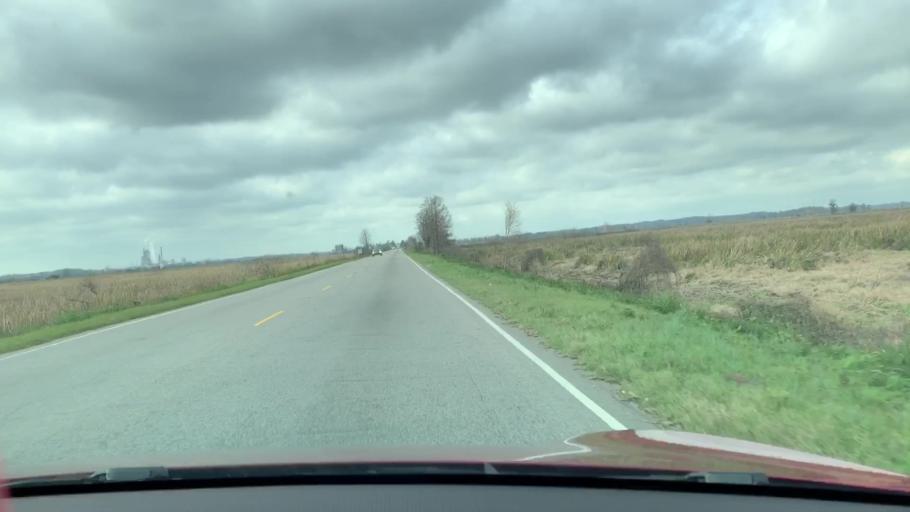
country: US
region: Georgia
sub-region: Chatham County
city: Port Wentworth
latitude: 32.1660
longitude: -81.1222
